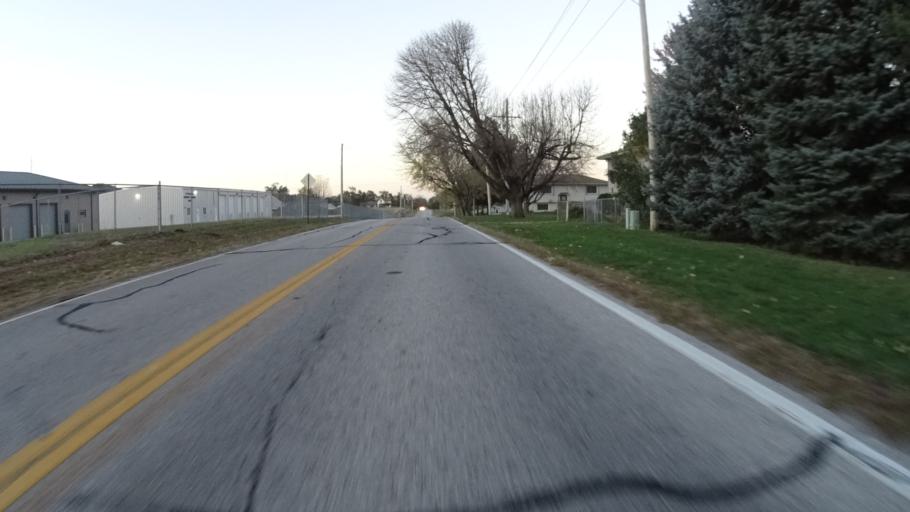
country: US
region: Nebraska
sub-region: Sarpy County
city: Offutt Air Force Base
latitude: 41.1698
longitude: -95.9526
